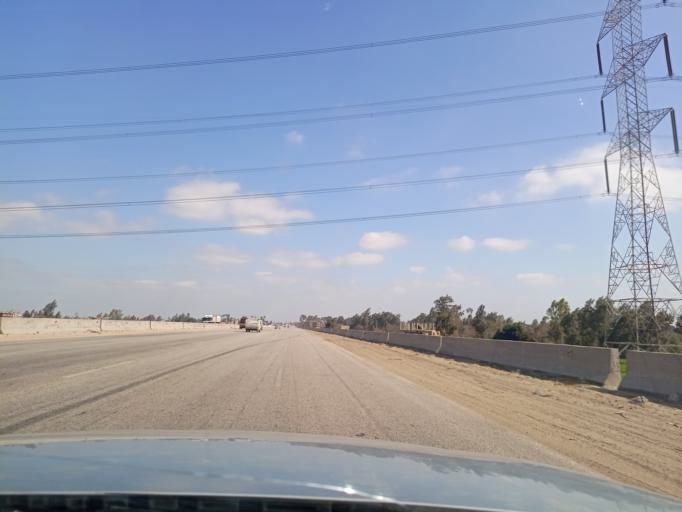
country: EG
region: Muhafazat al Qalyubiyah
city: Banha
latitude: 30.4409
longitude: 31.1133
